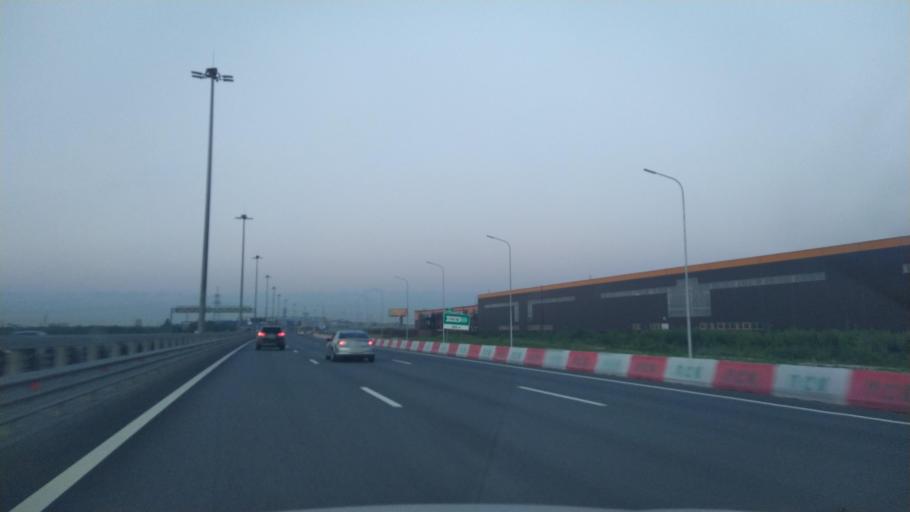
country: RU
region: Leningrad
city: Parnas
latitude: 60.0944
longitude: 30.3514
